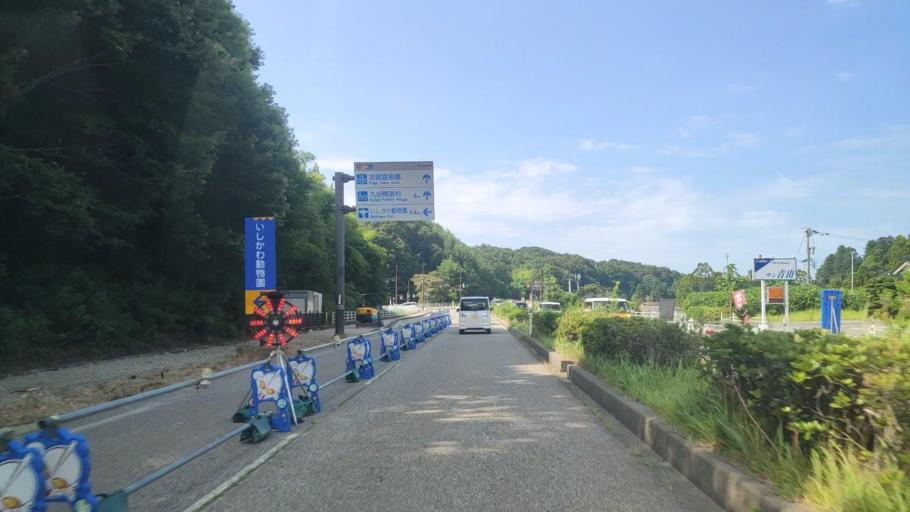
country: JP
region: Ishikawa
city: Matsuto
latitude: 36.4370
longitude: 136.5429
